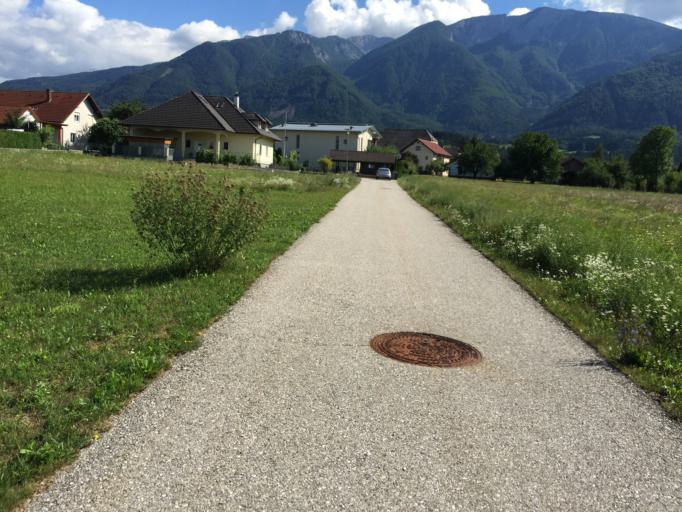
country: AT
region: Carinthia
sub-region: Politischer Bezirk Volkermarkt
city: Feistritz ob Bleiburg
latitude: 46.5634
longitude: 14.7622
